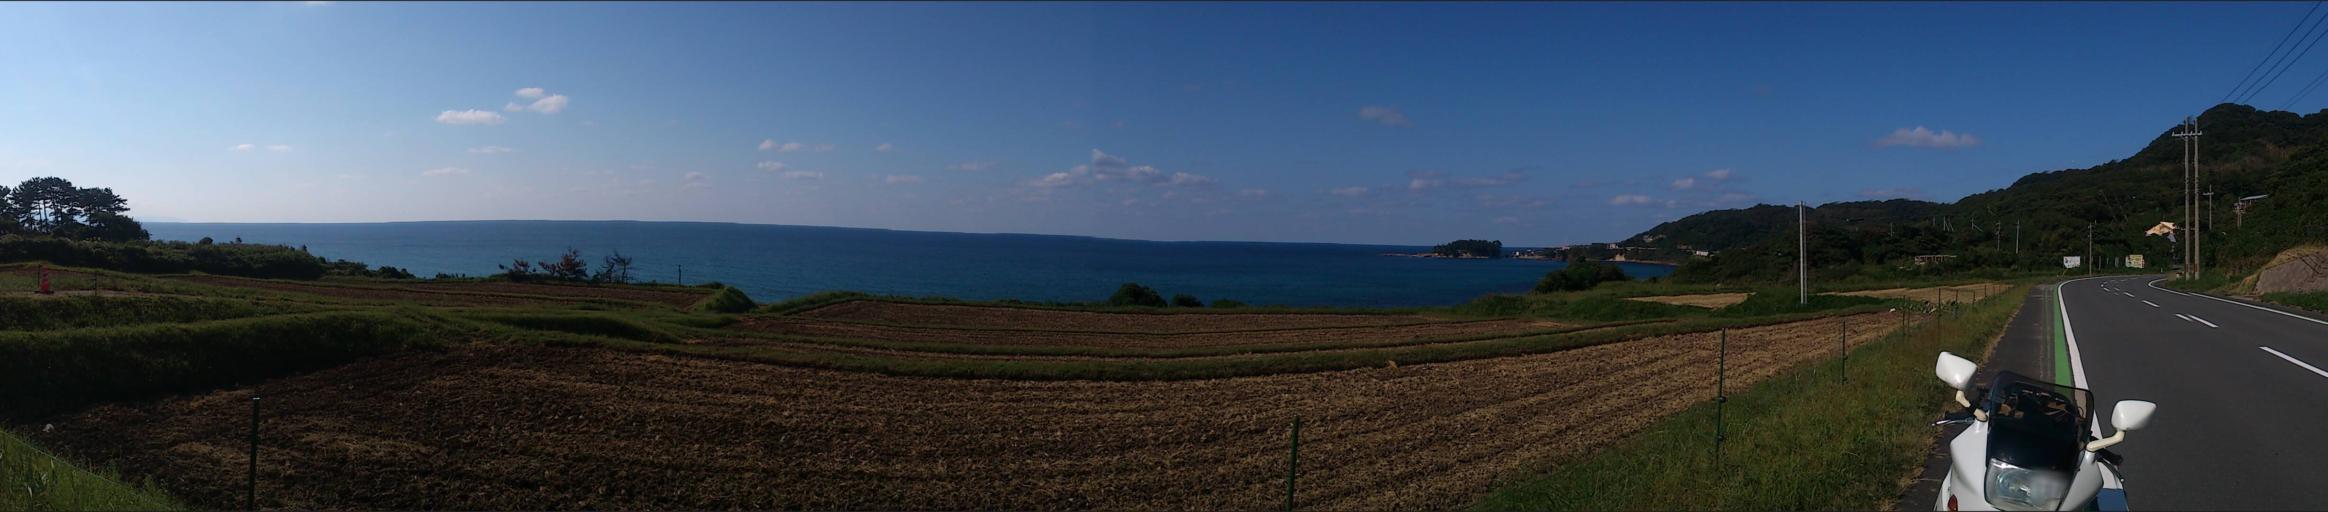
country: JP
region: Kyoto
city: Miyazu
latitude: 35.7234
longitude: 135.0844
